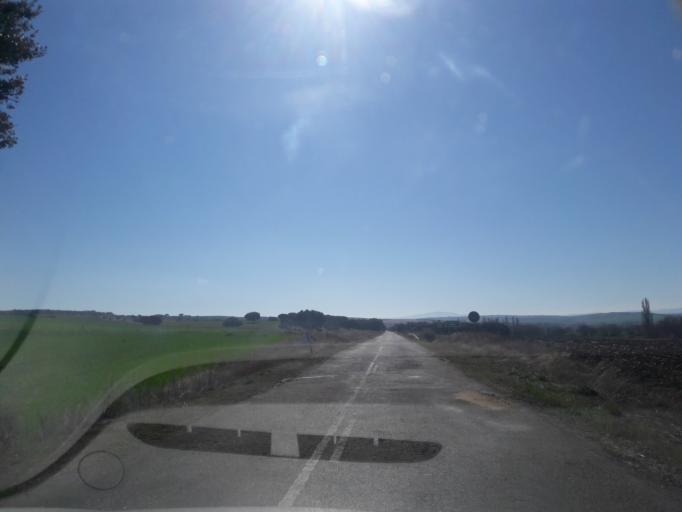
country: ES
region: Castille and Leon
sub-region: Provincia de Avila
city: Mancera de Arriba
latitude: 40.8135
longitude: -5.1645
